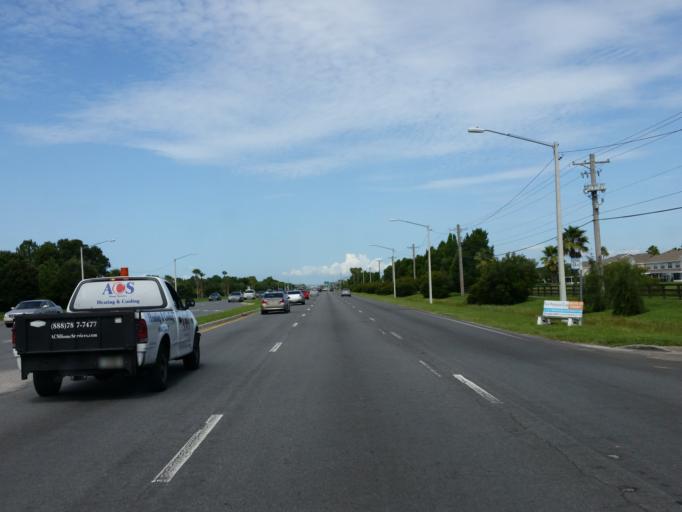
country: US
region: Florida
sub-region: Hillsborough County
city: Brandon
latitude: 27.9234
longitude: -82.3068
